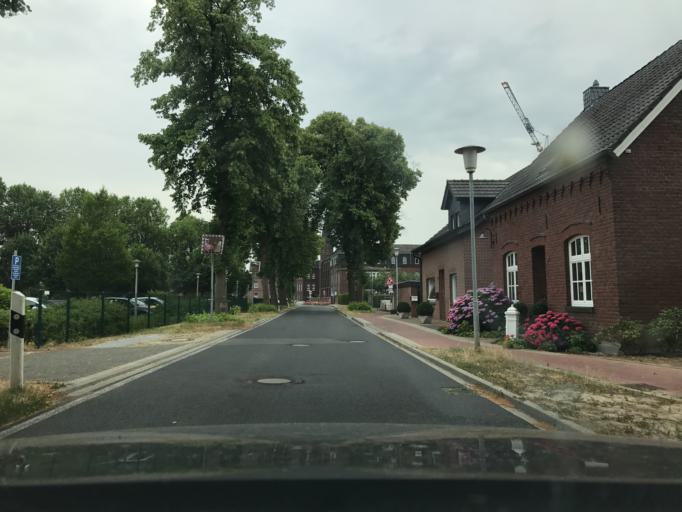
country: DE
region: North Rhine-Westphalia
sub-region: Regierungsbezirk Dusseldorf
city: Grefrath
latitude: 51.3458
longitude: 6.3644
